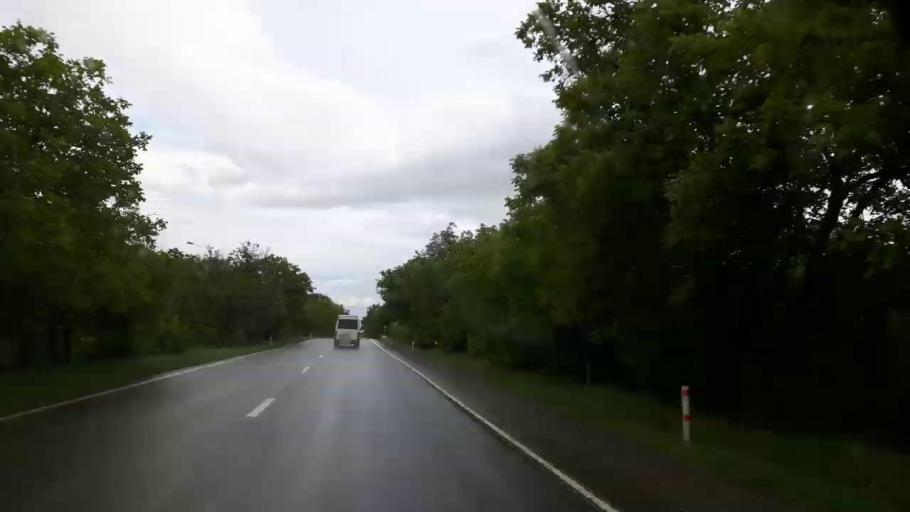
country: GE
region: Shida Kartli
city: Kaspi
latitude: 41.9593
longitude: 44.4817
